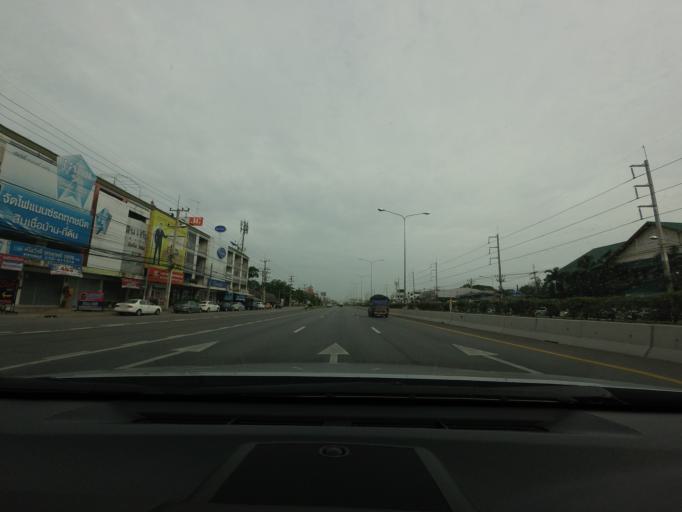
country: TH
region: Phetchaburi
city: Phetchaburi
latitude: 13.1075
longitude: 99.9336
